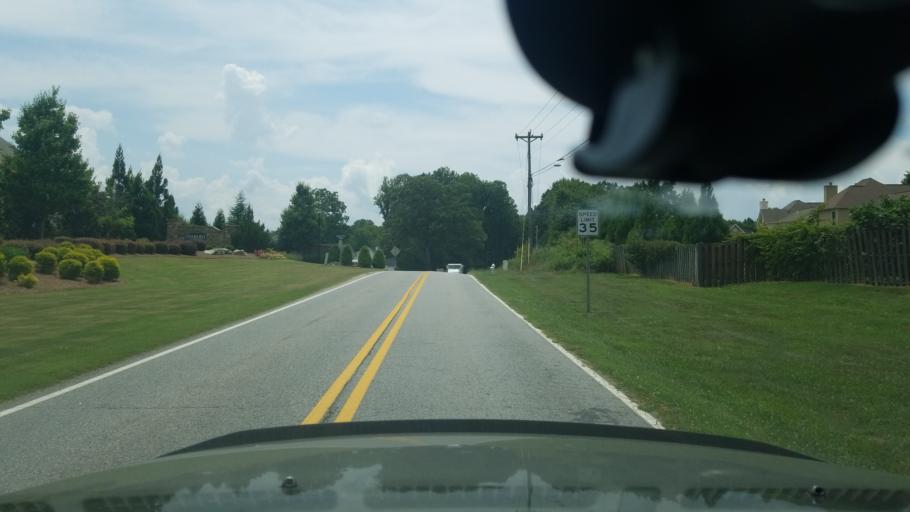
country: US
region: Georgia
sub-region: Forsyth County
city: Cumming
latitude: 34.2189
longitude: -84.2005
